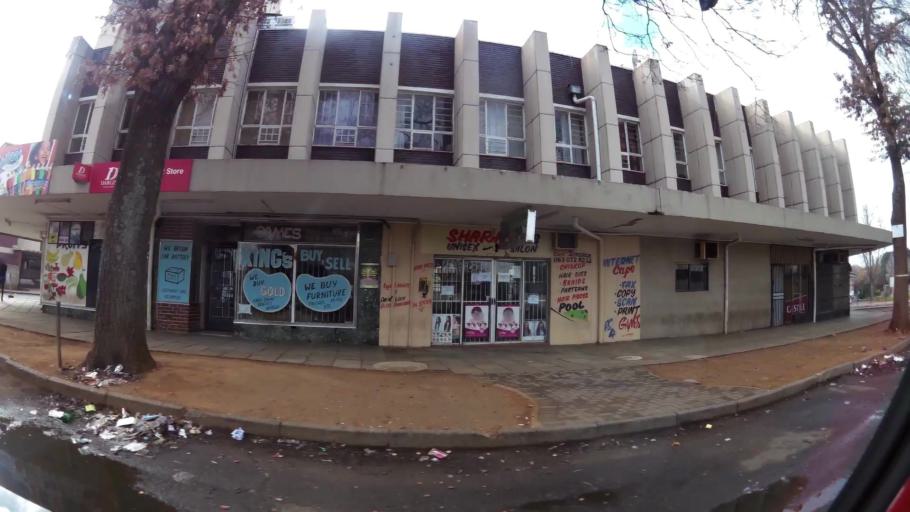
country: ZA
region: Gauteng
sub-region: Sedibeng District Municipality
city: Vanderbijlpark
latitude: -26.6942
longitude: 27.8253
